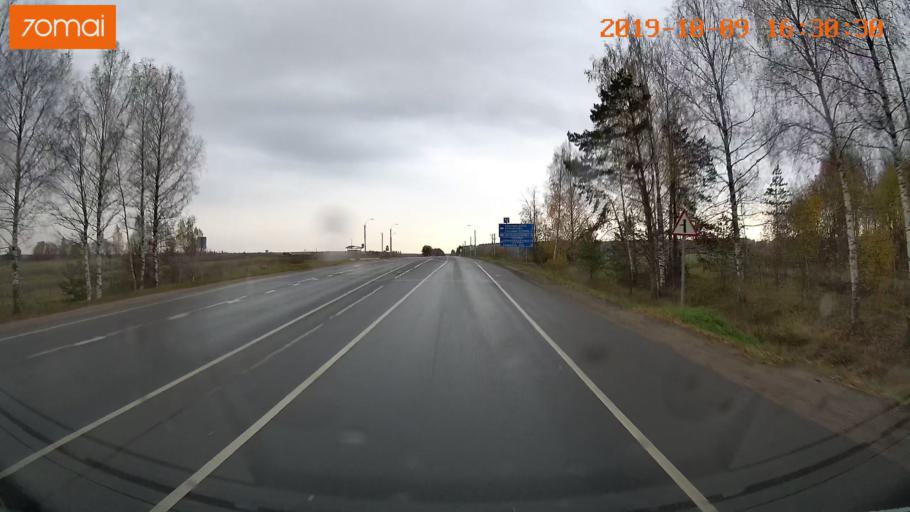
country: RU
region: Kostroma
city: Oktyabr'skiy
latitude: 57.6185
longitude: 40.9407
